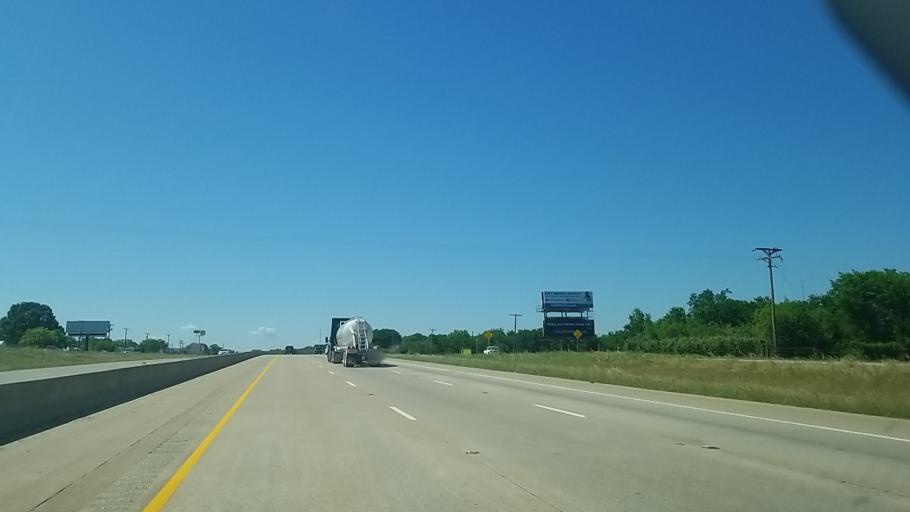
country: US
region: Texas
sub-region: Navarro County
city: Corsicana
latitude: 32.2384
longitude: -96.4933
